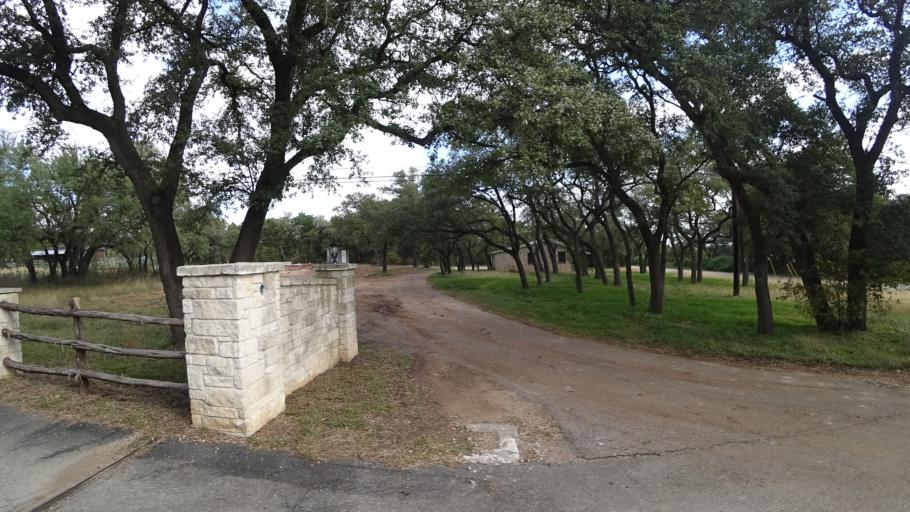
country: US
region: Texas
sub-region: Travis County
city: Bee Cave
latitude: 30.2493
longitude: -97.9222
